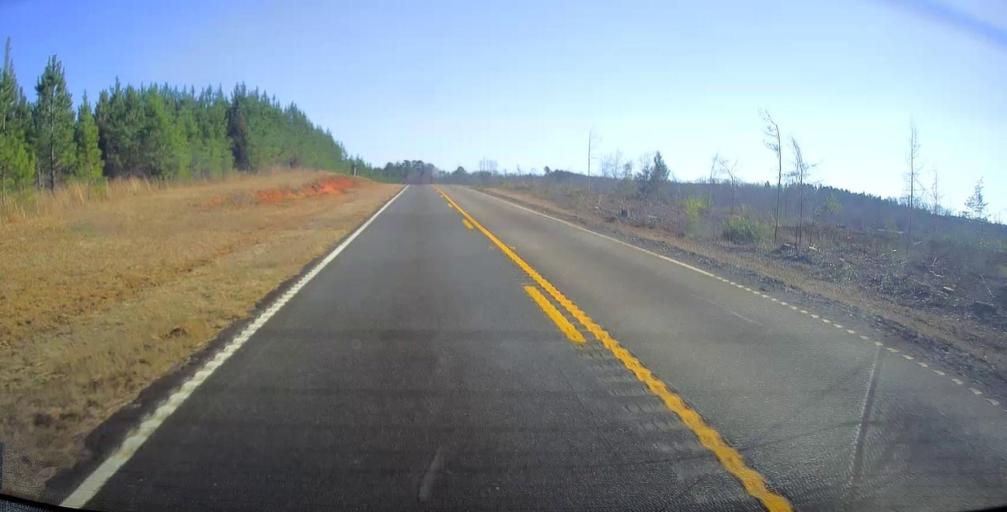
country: US
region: Georgia
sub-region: Talbot County
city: Talbotton
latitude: 32.6569
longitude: -84.4582
